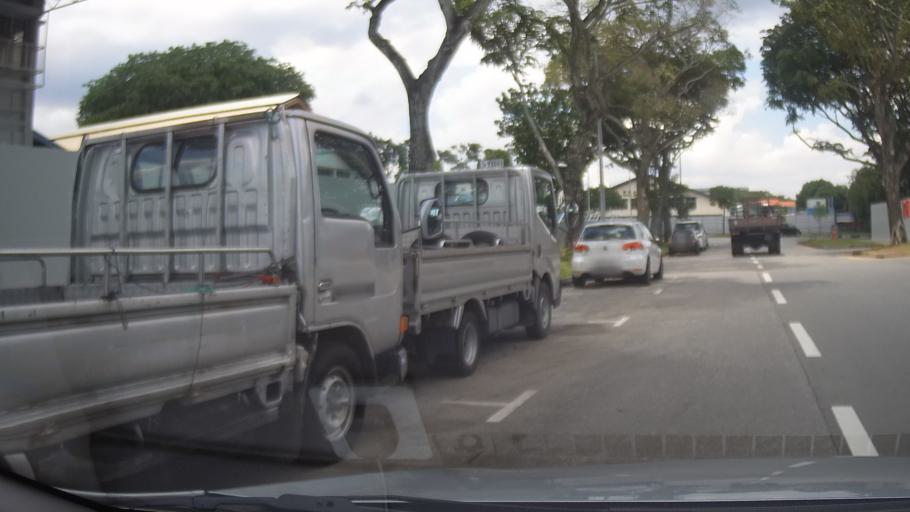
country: MY
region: Johor
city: Johor Bahru
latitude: 1.3269
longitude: 103.6898
